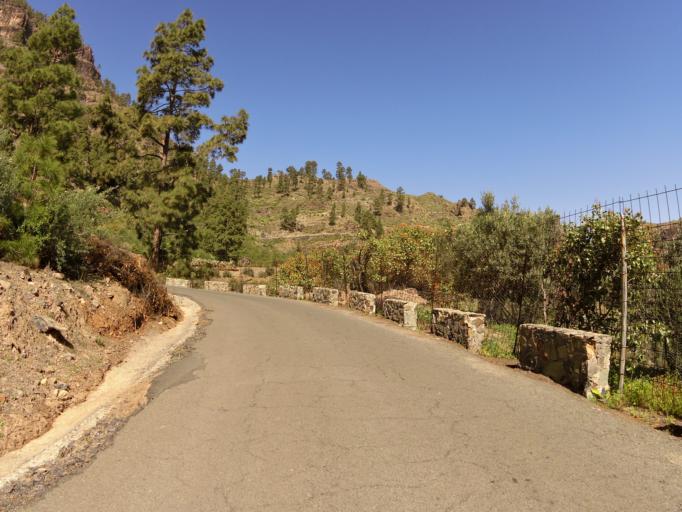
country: ES
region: Canary Islands
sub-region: Provincia de Las Palmas
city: Mogan
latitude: 27.8970
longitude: -15.6839
